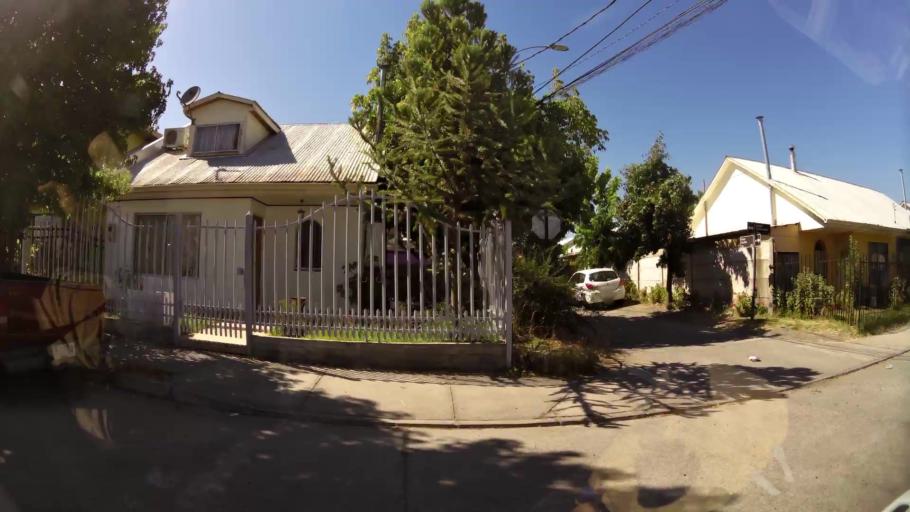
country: CL
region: Maule
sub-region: Provincia de Curico
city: Curico
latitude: -34.9692
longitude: -71.2549
